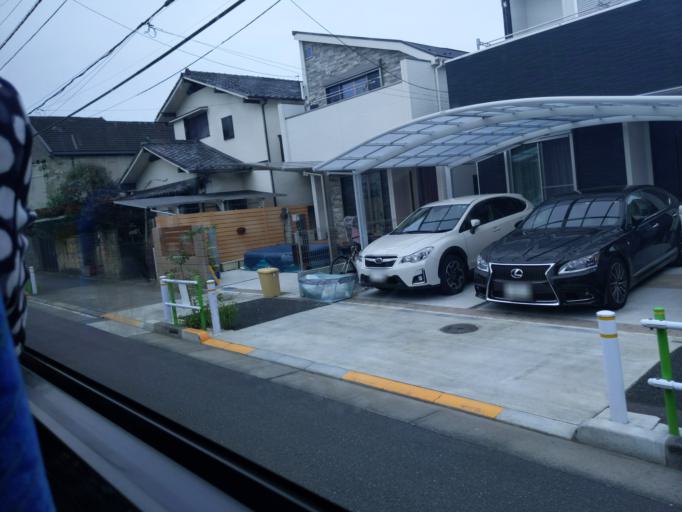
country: JP
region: Saitama
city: Wako
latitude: 35.7900
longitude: 139.6490
